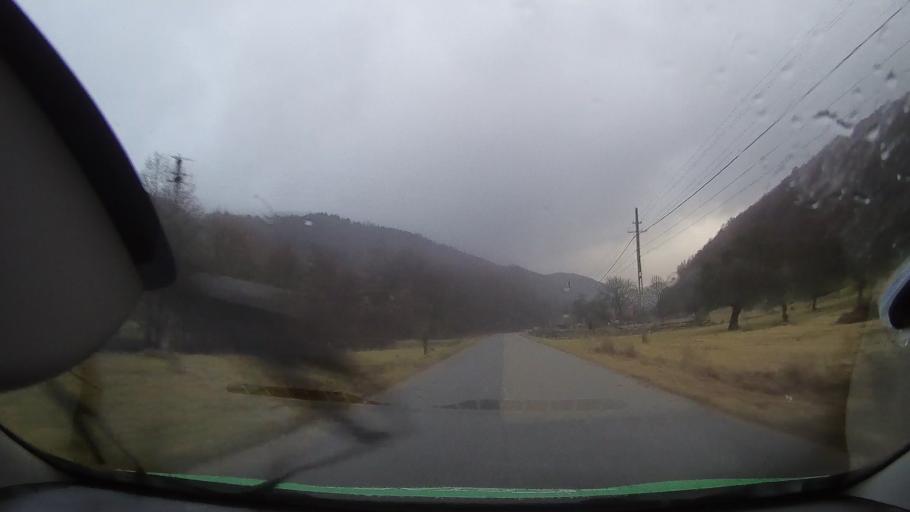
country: RO
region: Hunedoara
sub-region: Comuna Ribita
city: Ribita
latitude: 46.2591
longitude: 22.7452
